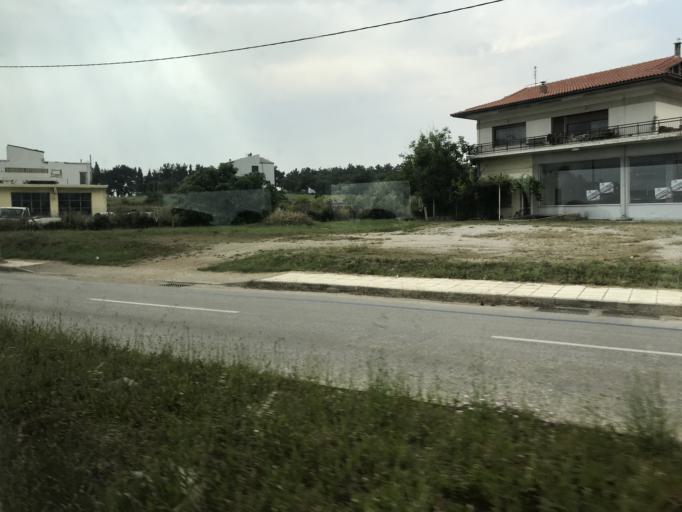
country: GR
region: East Macedonia and Thrace
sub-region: Nomos Evrou
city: Alexandroupoli
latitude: 40.8521
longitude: 25.9064
